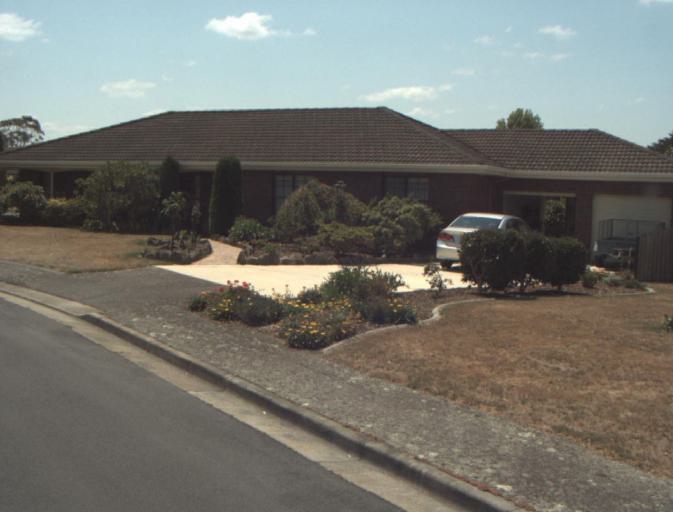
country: AU
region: Tasmania
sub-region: Launceston
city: Newstead
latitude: -41.4686
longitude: 147.1829
